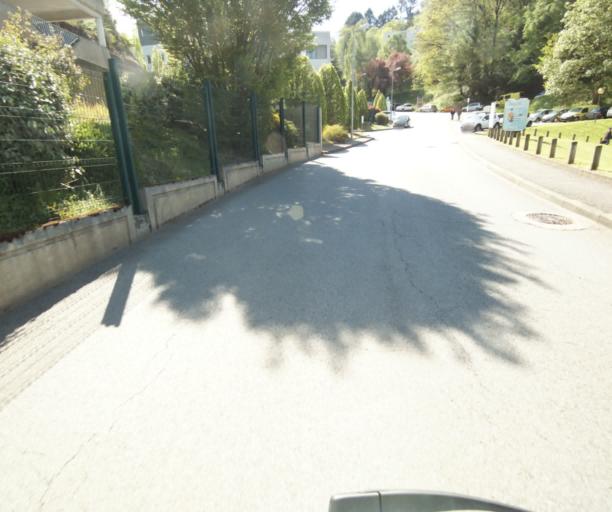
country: FR
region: Limousin
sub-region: Departement de la Correze
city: Tulle
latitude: 45.2655
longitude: 1.7745
